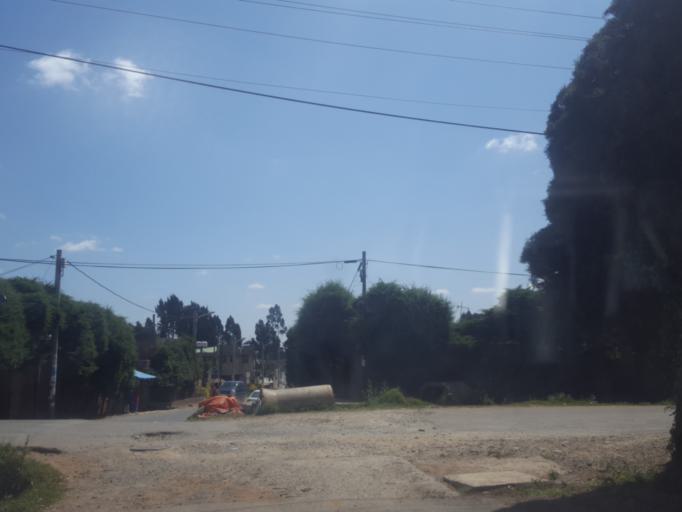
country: ET
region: Adis Abeba
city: Addis Ababa
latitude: 9.0561
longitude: 38.7368
